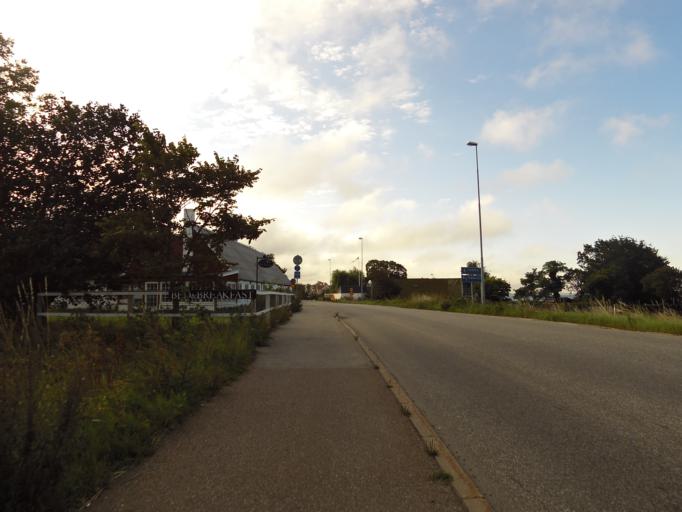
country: SE
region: Skane
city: Bjarred
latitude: 55.7081
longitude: 13.0359
